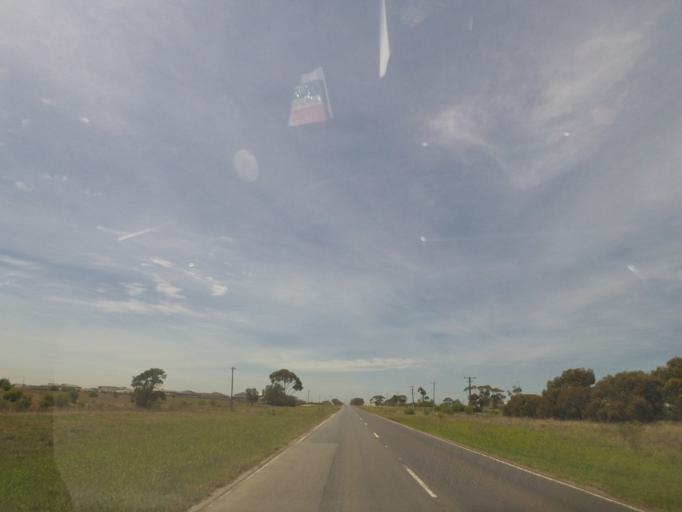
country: AU
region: Victoria
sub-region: Wyndham
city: Wyndham Vale
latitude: -37.8508
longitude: 144.5825
